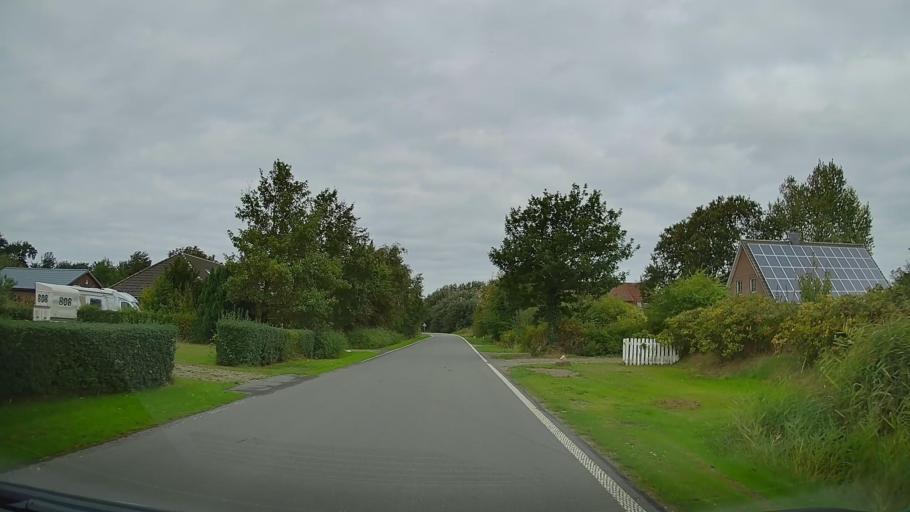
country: DE
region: Schleswig-Holstein
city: Klanxbull
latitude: 54.8845
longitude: 8.6824
